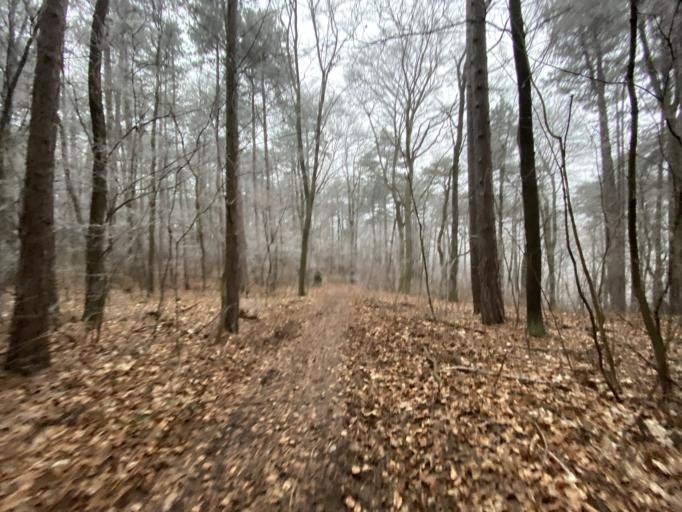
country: AT
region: Lower Austria
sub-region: Politischer Bezirk Baden
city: Baden
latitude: 47.9988
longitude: 16.1957
